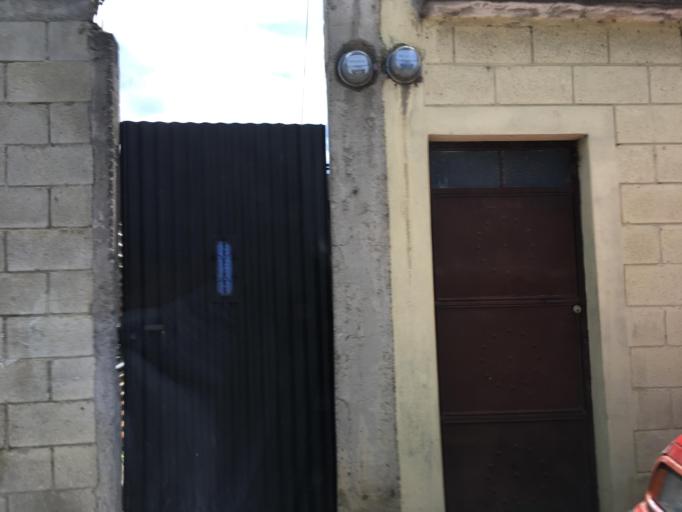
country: GT
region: Sacatepequez
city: Ciudad Vieja
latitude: 14.5256
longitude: -90.7486
